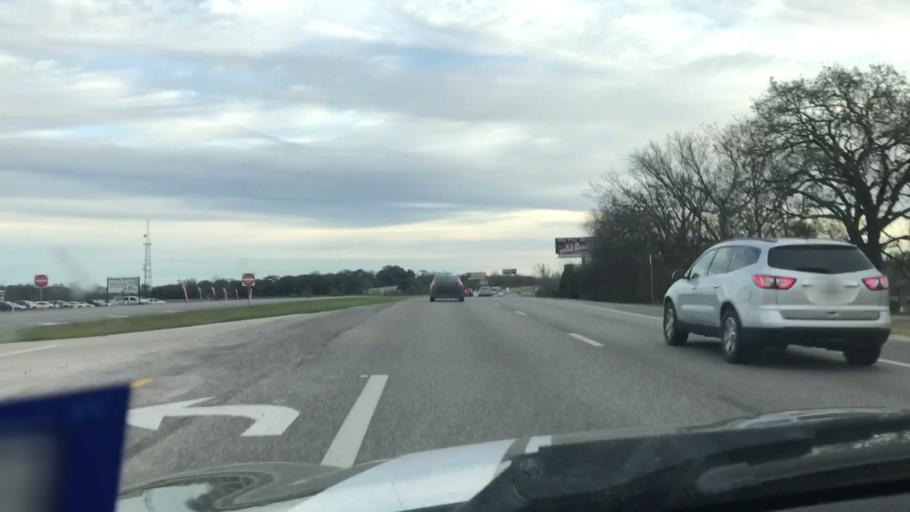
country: US
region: Texas
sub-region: Waller County
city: Hempstead
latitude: 30.1301
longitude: -96.1416
